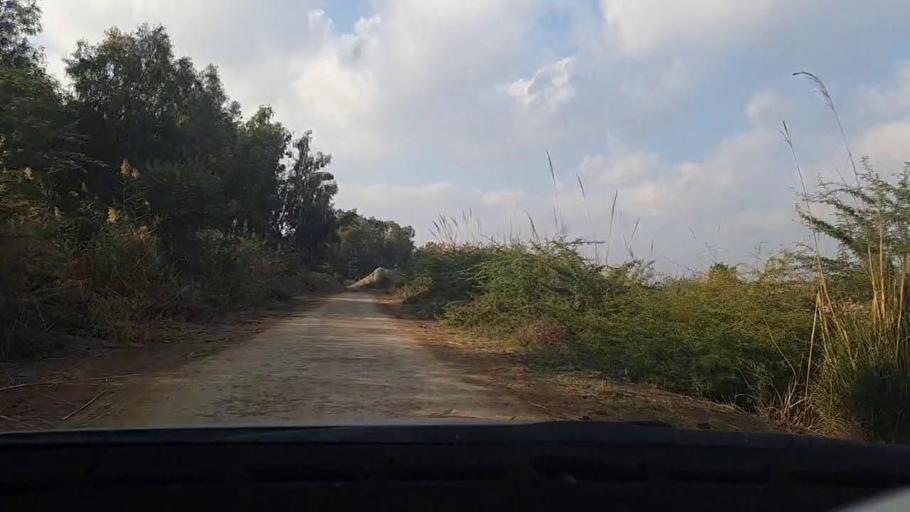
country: PK
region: Sindh
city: Tando Mittha Khan
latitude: 25.9117
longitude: 69.3040
